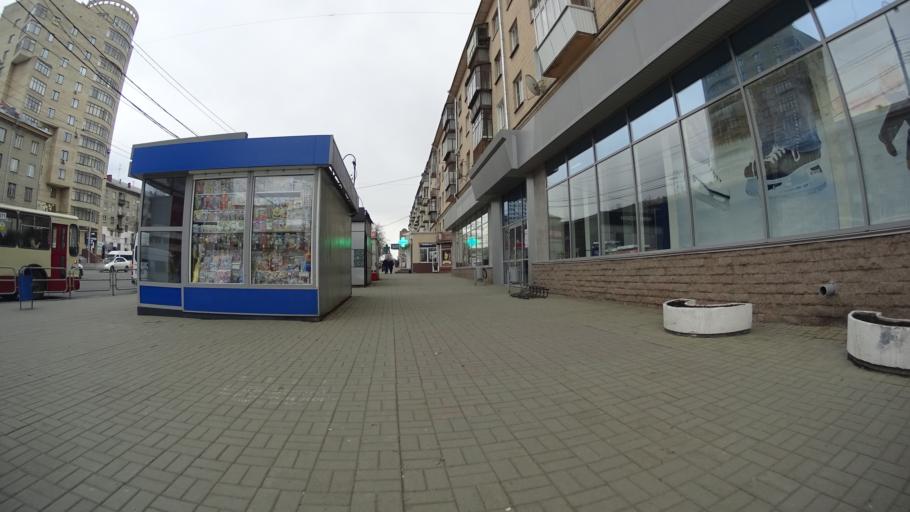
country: RU
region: Chelyabinsk
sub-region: Gorod Chelyabinsk
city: Chelyabinsk
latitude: 55.1610
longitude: 61.4205
